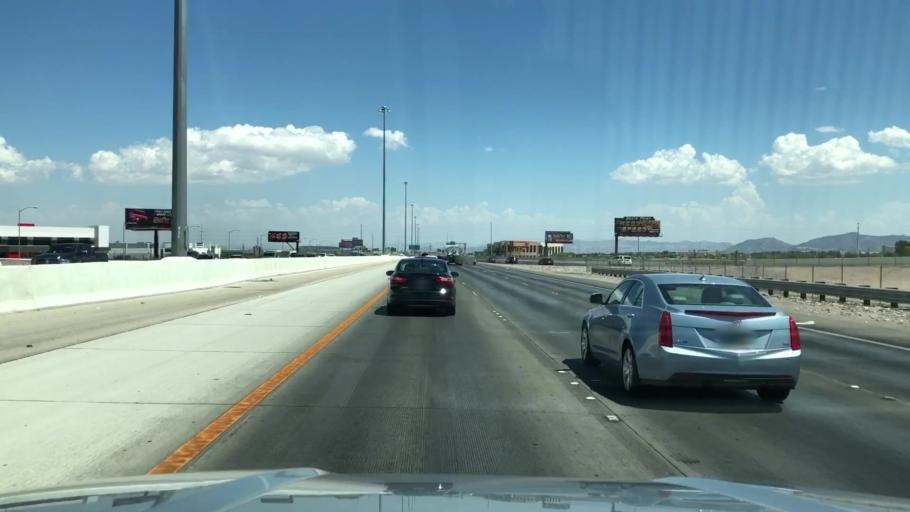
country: US
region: Nevada
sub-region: Clark County
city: Enterprise
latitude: 36.0670
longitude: -115.2224
